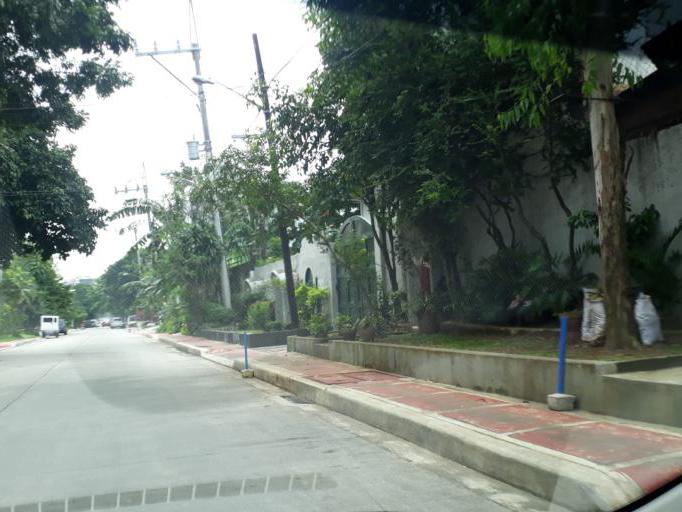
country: PH
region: Calabarzon
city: Del Monte
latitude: 14.6341
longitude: 121.0314
